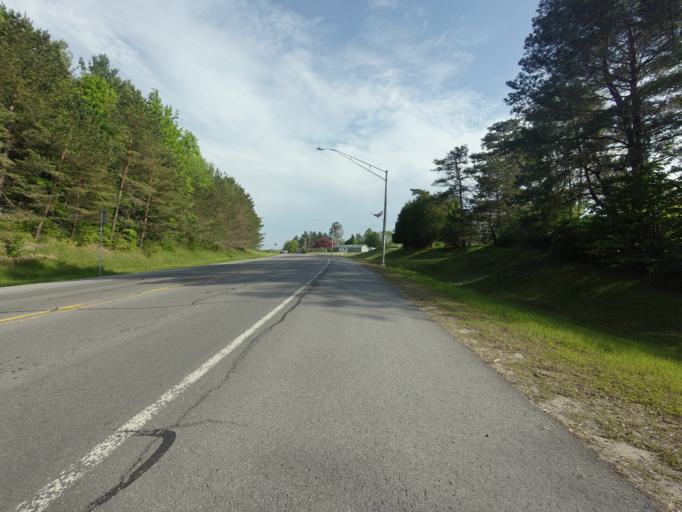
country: US
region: New York
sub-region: St. Lawrence County
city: Gouverneur
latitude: 44.1568
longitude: -75.3168
